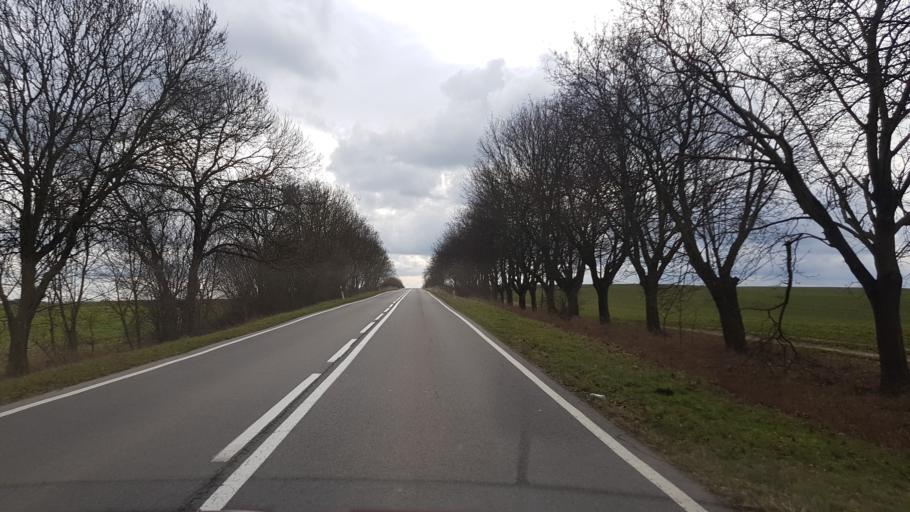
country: PL
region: West Pomeranian Voivodeship
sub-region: Powiat gryfinski
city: Banie
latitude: 53.1523
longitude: 14.6058
